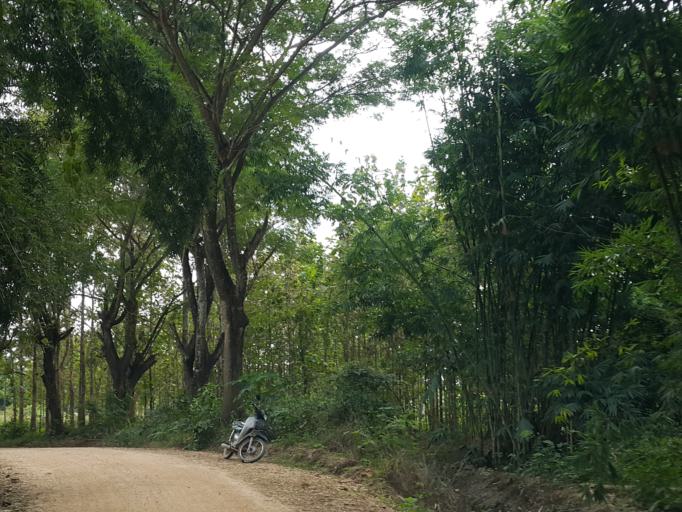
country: TH
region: Lampang
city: Hang Chat
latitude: 18.4754
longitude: 99.4132
